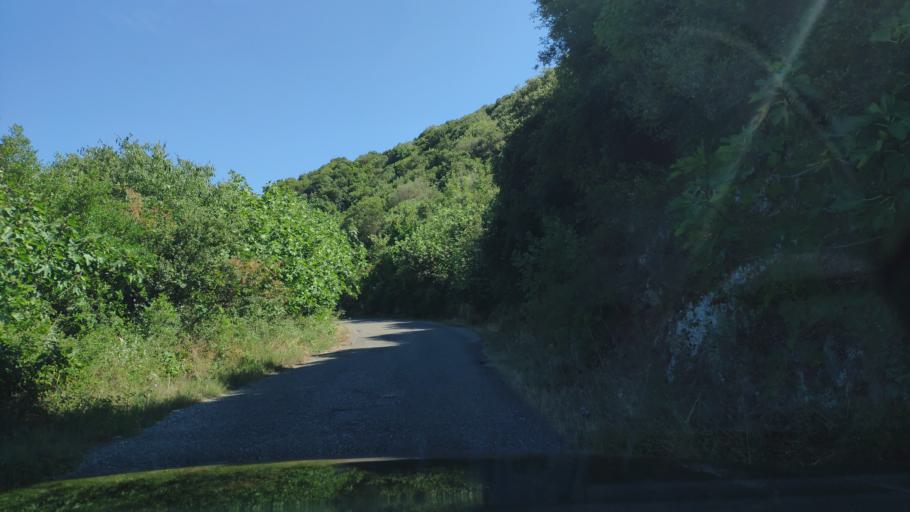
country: GR
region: West Greece
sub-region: Nomos Aitolias kai Akarnanias
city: Katouna
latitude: 38.8239
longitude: 21.1003
